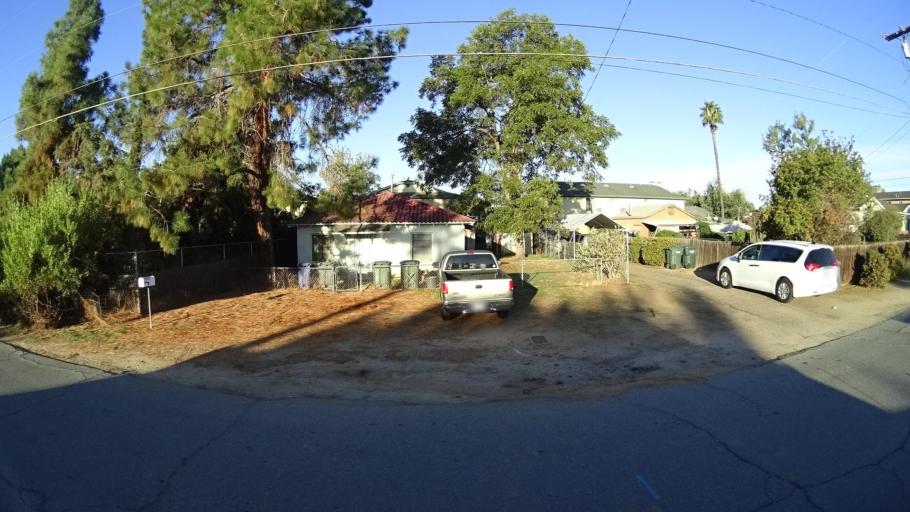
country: US
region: California
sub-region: San Diego County
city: Bostonia
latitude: 32.8110
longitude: -116.9379
